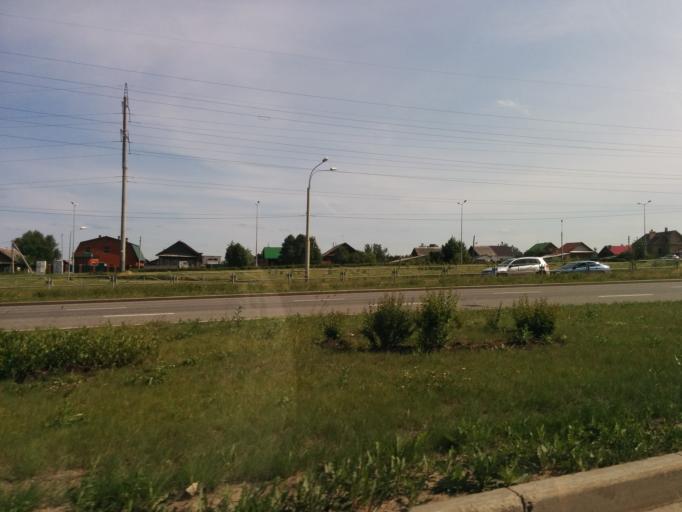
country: RU
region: Perm
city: Perm
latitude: 57.9987
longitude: 56.3110
